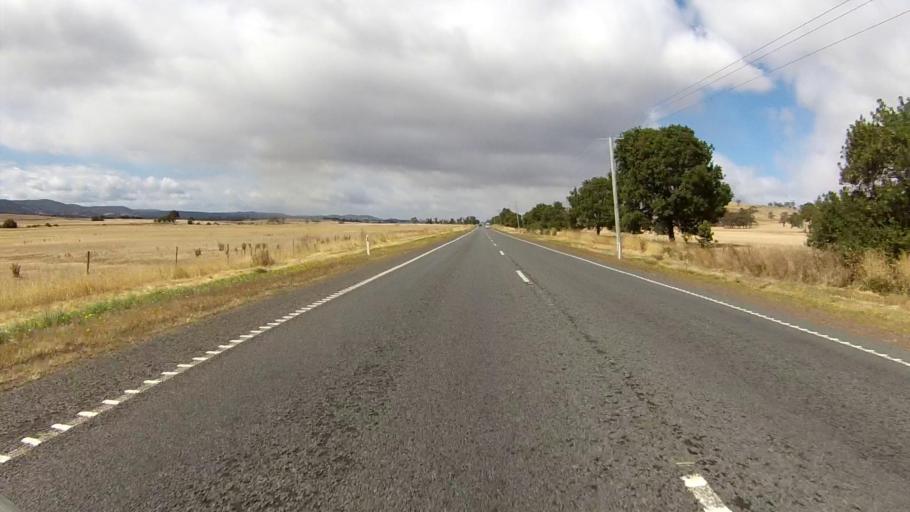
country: AU
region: Tasmania
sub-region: Northern Midlands
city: Evandale
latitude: -41.9667
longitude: 147.5004
